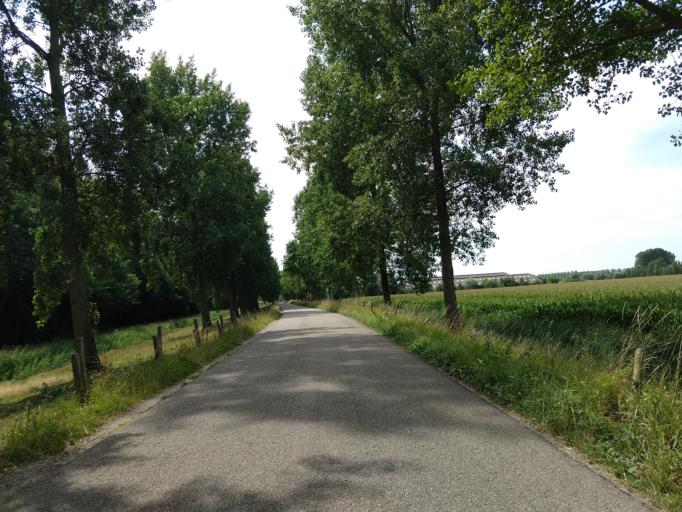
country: NL
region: Zeeland
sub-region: Gemeente Middelburg
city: Middelburg
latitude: 51.4767
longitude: 3.6828
